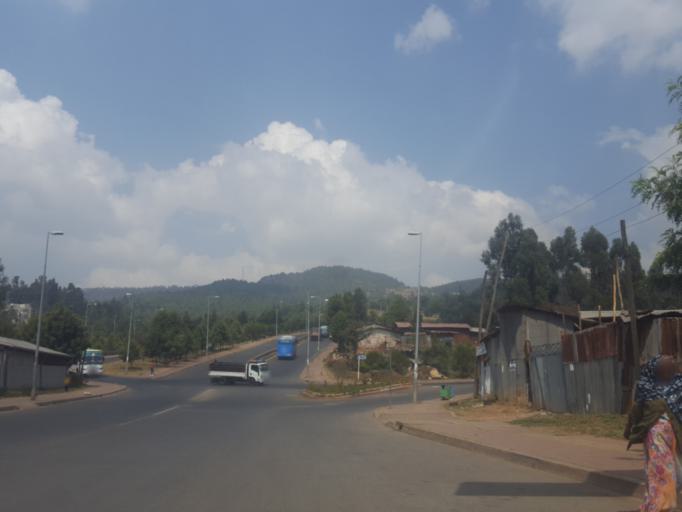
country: ET
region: Adis Abeba
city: Addis Ababa
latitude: 9.0669
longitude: 38.7214
